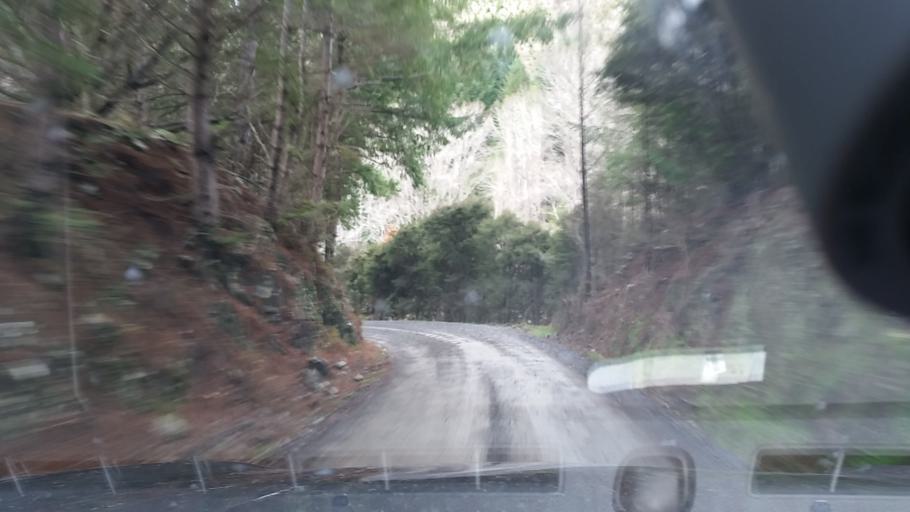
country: NZ
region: Tasman
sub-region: Tasman District
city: Richmond
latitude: -41.7299
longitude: 173.4685
